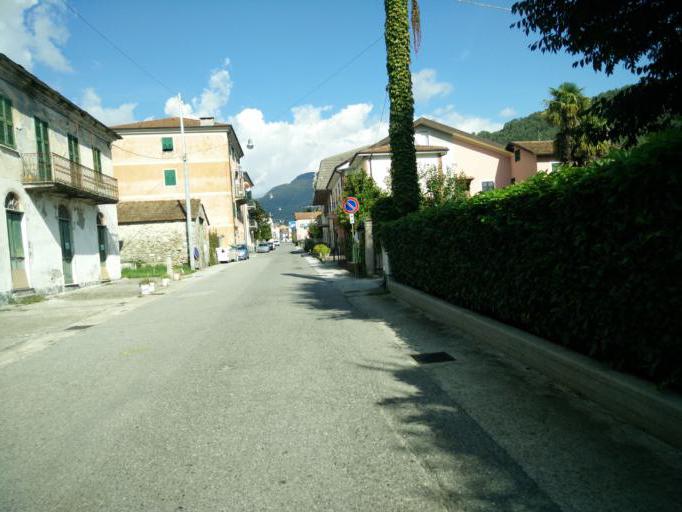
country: IT
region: Liguria
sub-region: Provincia di La Spezia
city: Sesta Godano
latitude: 44.2894
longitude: 9.6712
